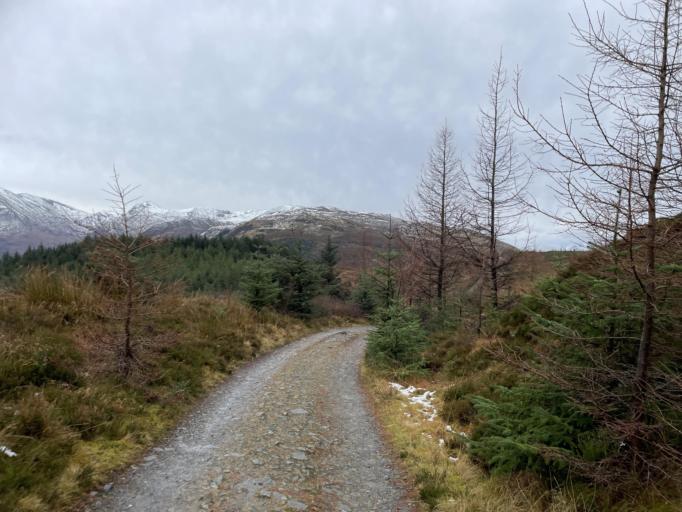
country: GB
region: Scotland
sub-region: Highland
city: Fort William
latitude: 56.8143
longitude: -5.0934
